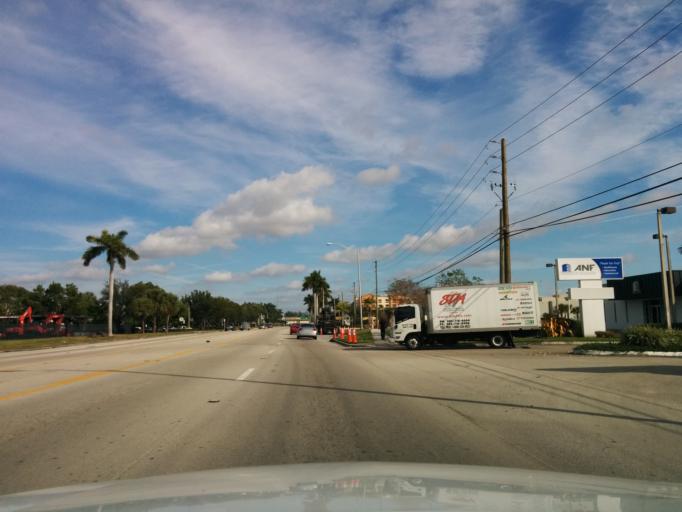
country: US
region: Florida
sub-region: Broward County
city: Broadview Park
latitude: 26.0877
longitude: -80.2284
